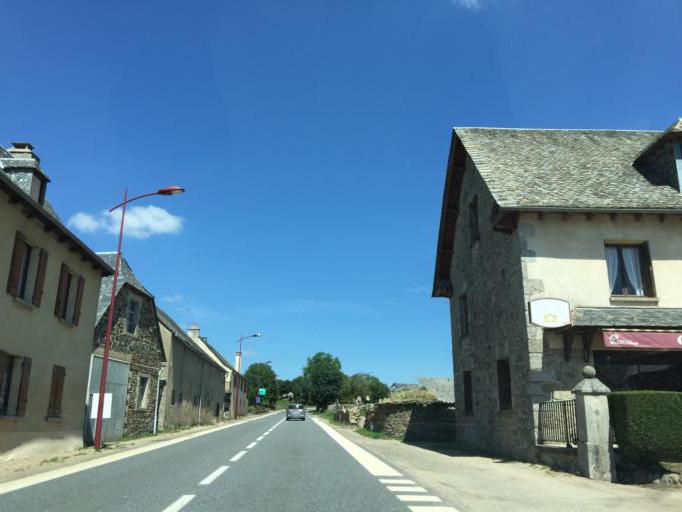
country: FR
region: Midi-Pyrenees
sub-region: Departement de l'Aveyron
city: Laguiole
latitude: 44.6118
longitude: 2.8066
